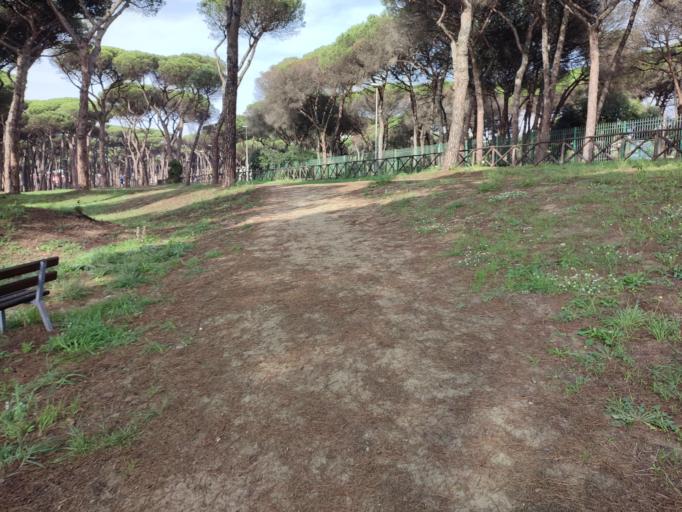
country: IT
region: Latium
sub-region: Citta metropolitana di Roma Capitale
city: Lido di Ostia
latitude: 41.7308
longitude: 12.2996
